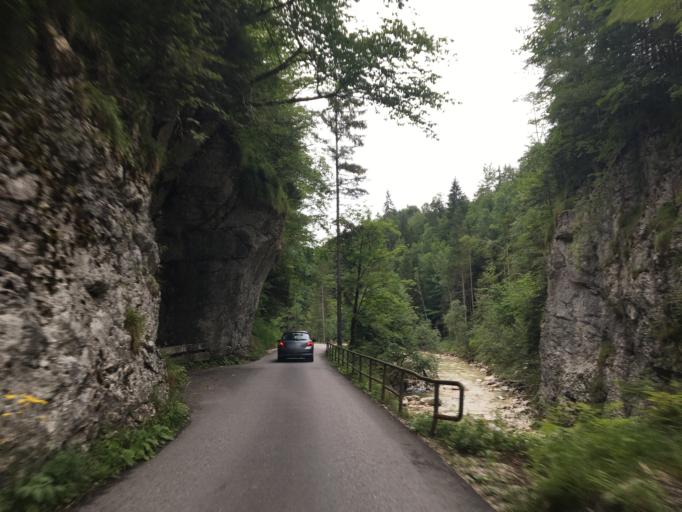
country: AT
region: Salzburg
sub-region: Politischer Bezirk Salzburg-Umgebung
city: Strobl
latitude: 47.7005
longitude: 13.4932
